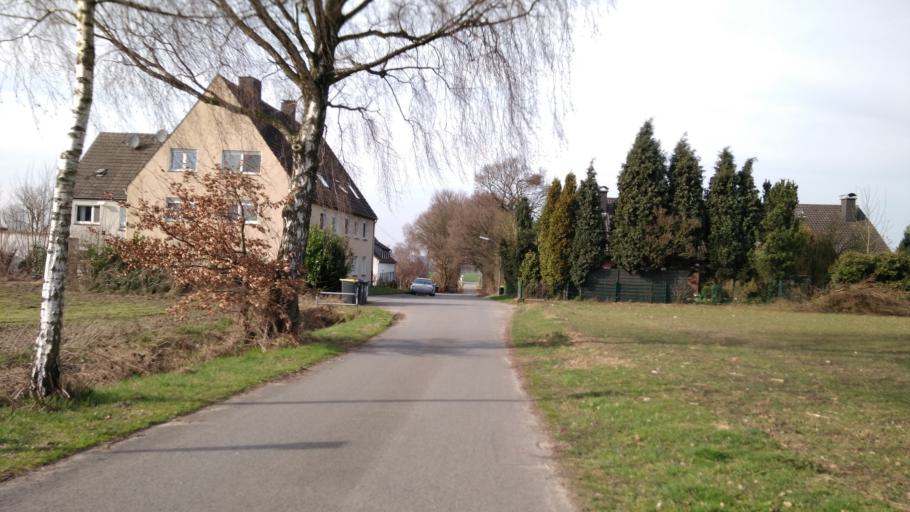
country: DE
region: North Rhine-Westphalia
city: Herten
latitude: 51.6236
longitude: 7.1639
